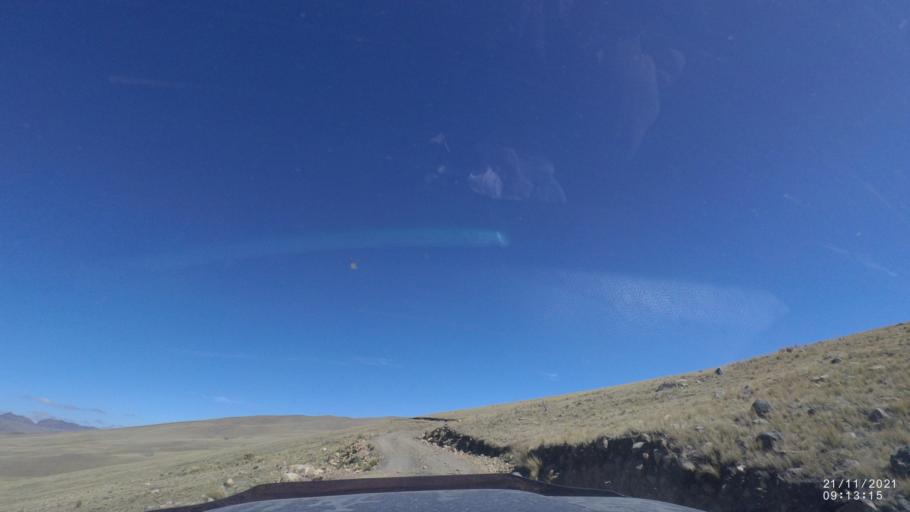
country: BO
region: Cochabamba
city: Cochabamba
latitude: -17.1416
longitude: -66.2571
